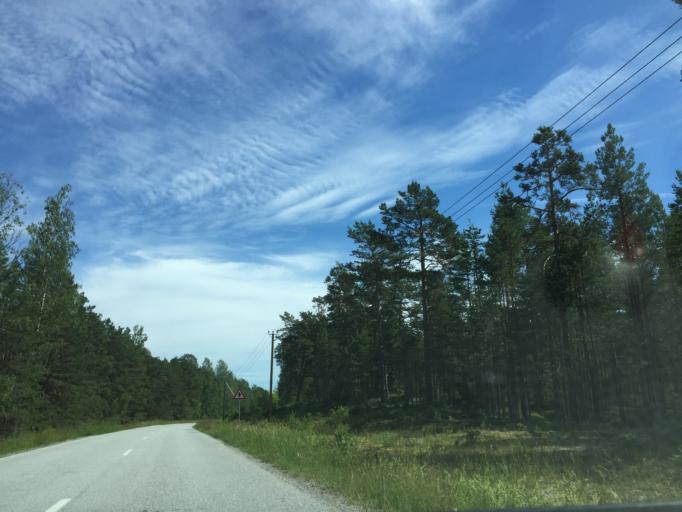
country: LV
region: Rojas
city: Roja
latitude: 57.5702
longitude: 22.6441
